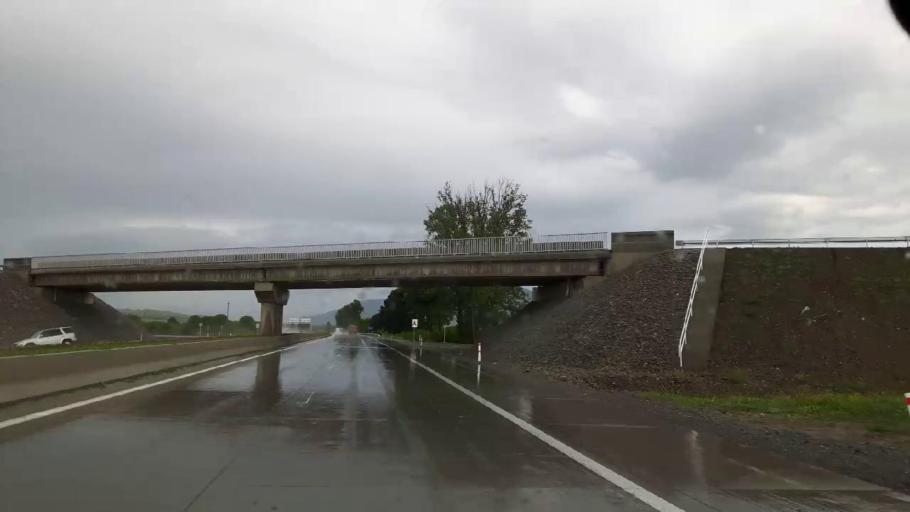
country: GE
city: Agara
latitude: 42.0316
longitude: 43.9497
